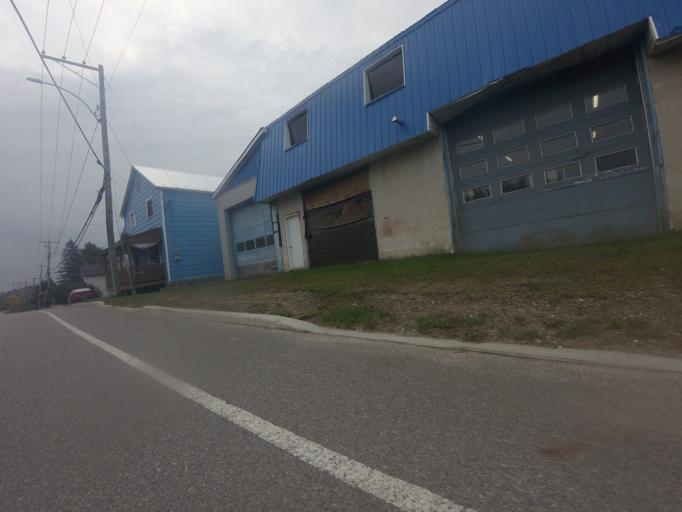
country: CA
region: Quebec
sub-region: Outaouais
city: Maniwaki
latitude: 46.0909
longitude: -76.0521
